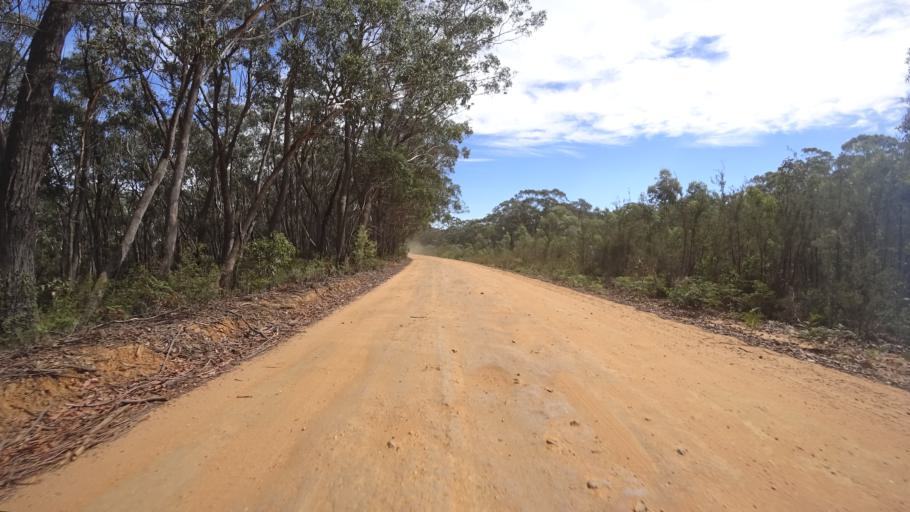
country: AU
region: New South Wales
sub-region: Lithgow
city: Lithgow
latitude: -33.3301
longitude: 150.2495
